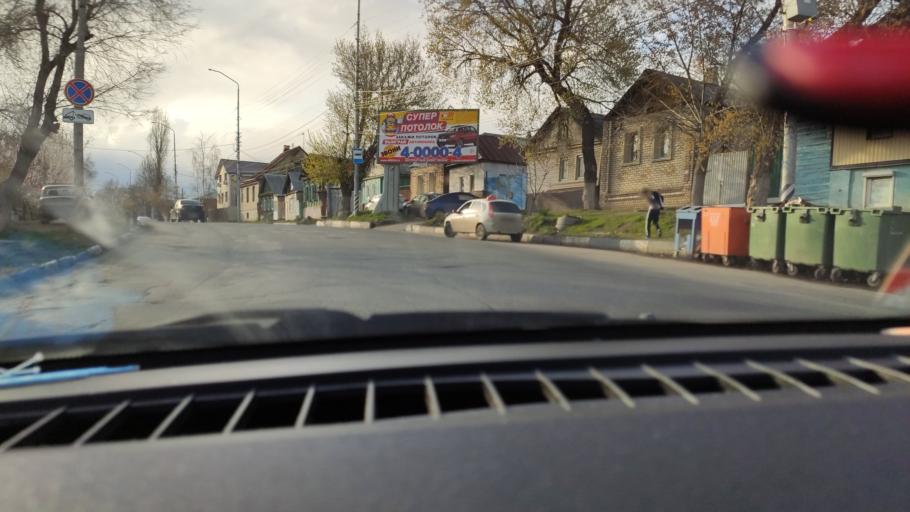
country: RU
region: Saratov
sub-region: Saratovskiy Rayon
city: Saratov
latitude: 51.5398
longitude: 46.0510
